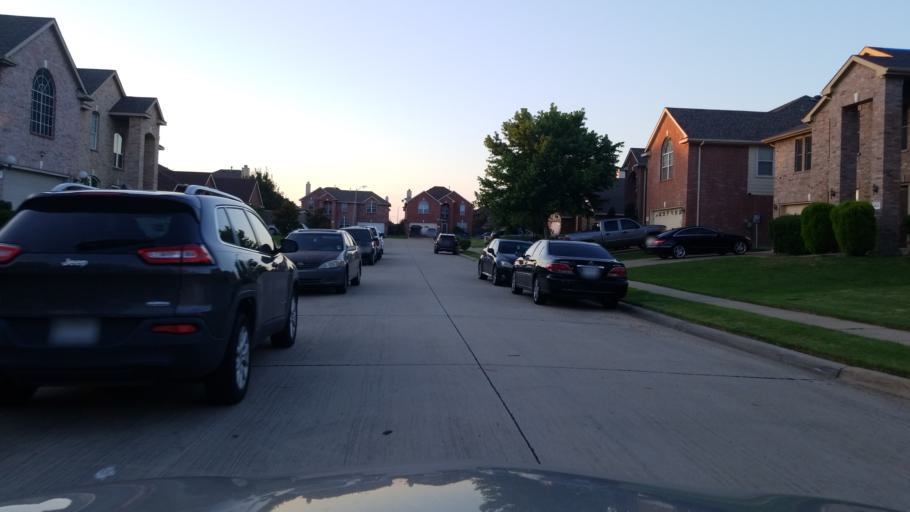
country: US
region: Texas
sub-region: Dallas County
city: Grand Prairie
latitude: 32.6855
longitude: -97.0378
